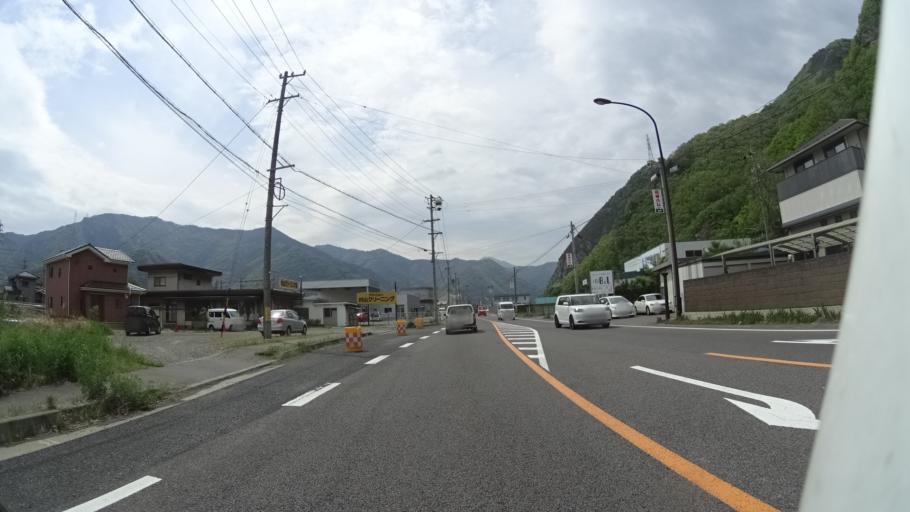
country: JP
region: Nagano
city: Ueda
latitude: 36.4191
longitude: 138.2052
